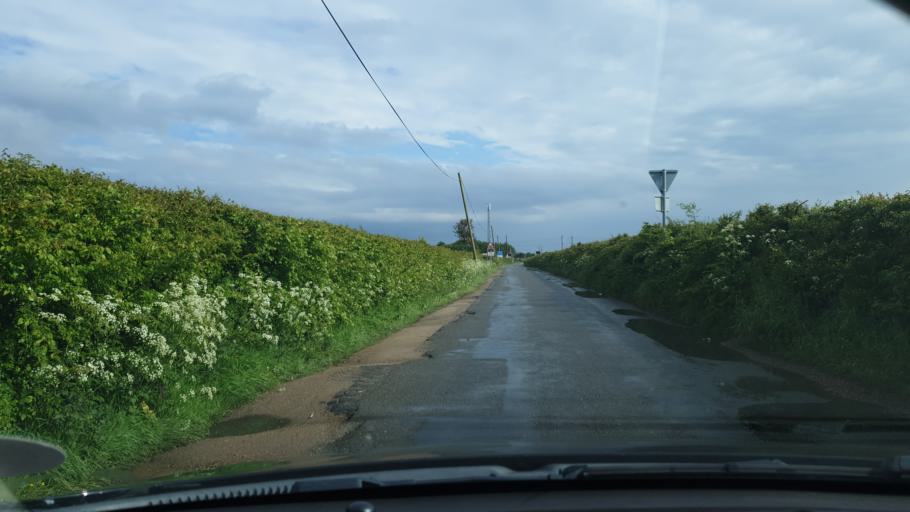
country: GB
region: England
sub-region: Essex
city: Great Bentley
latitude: 51.8511
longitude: 1.0440
